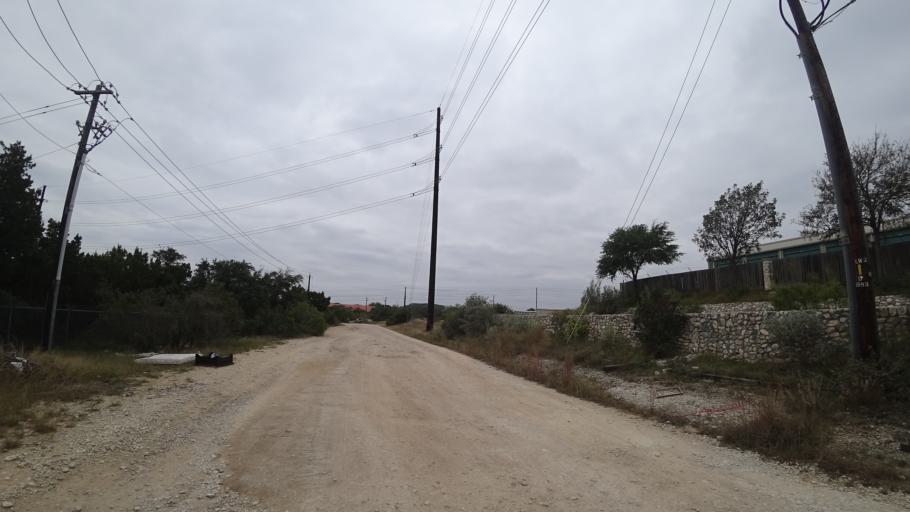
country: US
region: Texas
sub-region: Travis County
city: Lakeway
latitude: 30.3727
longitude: -97.9453
